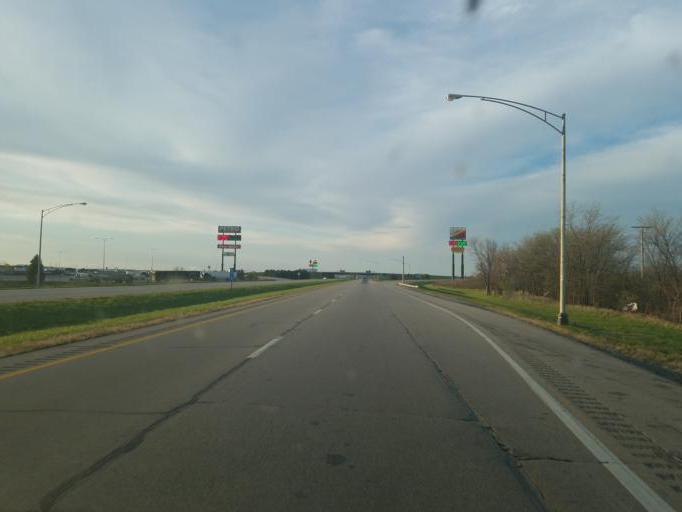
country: US
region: Ohio
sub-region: Wood County
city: Millbury
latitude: 41.5313
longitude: -83.4630
